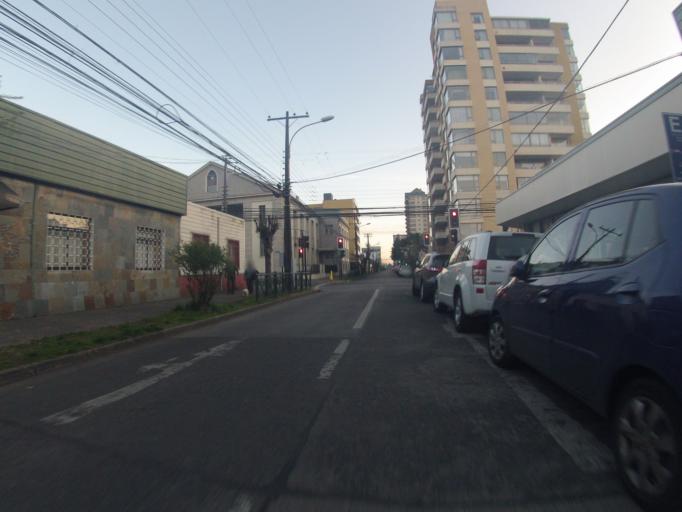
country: CL
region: Araucania
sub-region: Provincia de Cautin
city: Temuco
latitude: -38.7385
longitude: -72.5946
